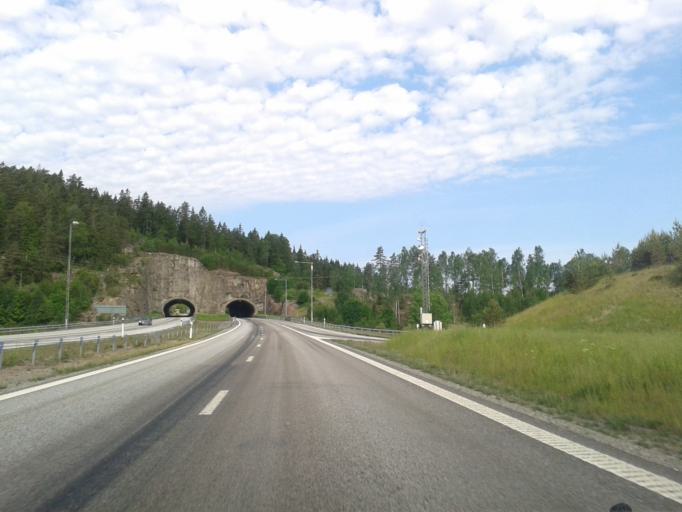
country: SE
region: Vaestra Goetaland
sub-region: Lysekils Kommun
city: Brastad
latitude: 58.5643
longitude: 11.4776
